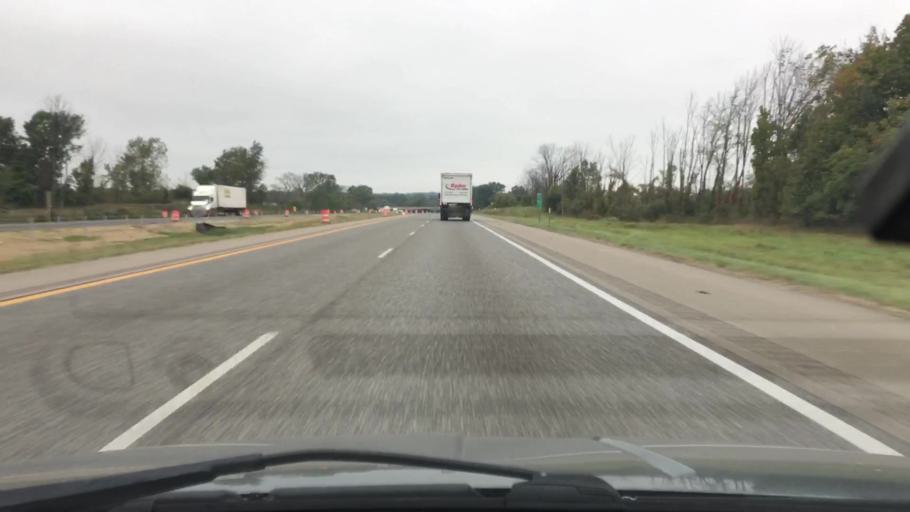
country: US
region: Michigan
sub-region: Van Buren County
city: Decatur
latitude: 42.1940
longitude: -86.0224
